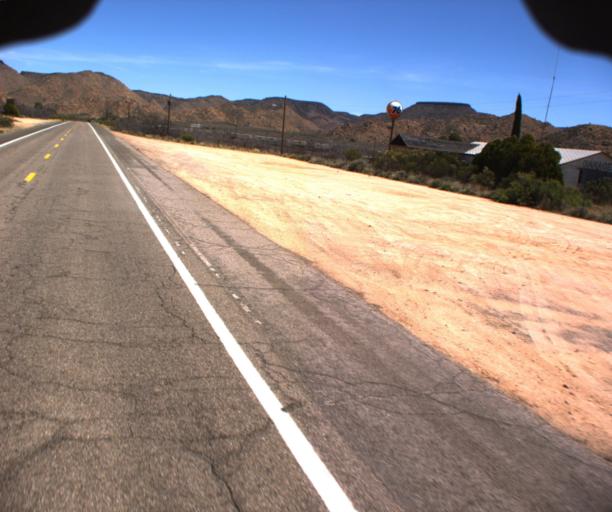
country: US
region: Arizona
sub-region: Mohave County
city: Peach Springs
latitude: 35.3637
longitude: -113.6833
